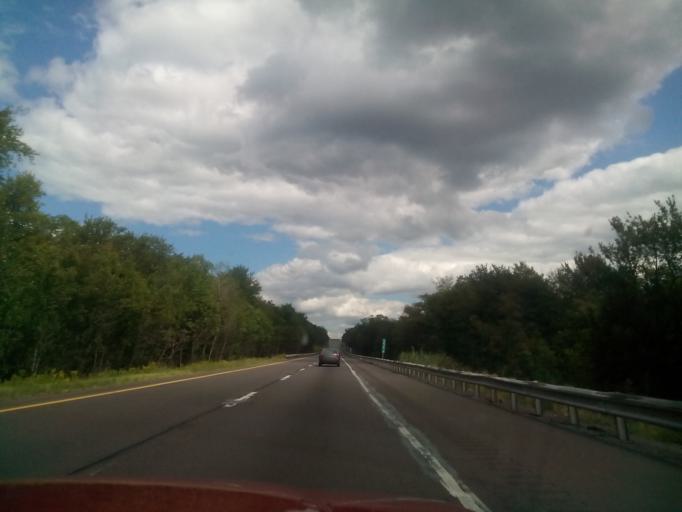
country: US
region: Pennsylvania
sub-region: Carbon County
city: Towamensing Trails
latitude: 41.0808
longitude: -75.6521
